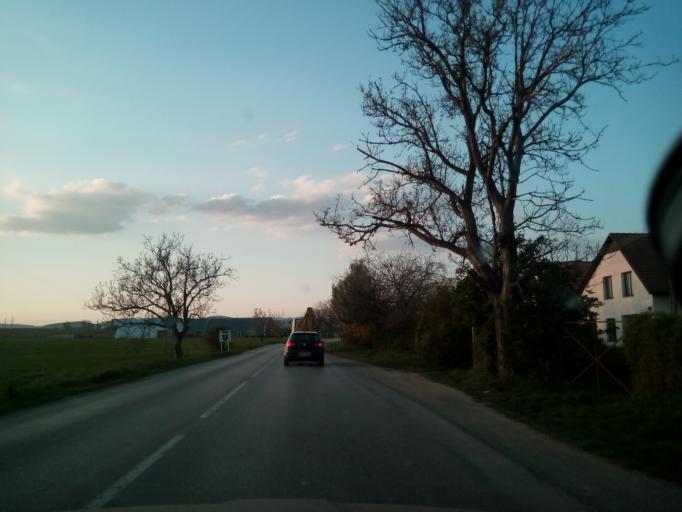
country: SK
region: Trnavsky
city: Vrbove
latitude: 48.5986
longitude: 17.7486
